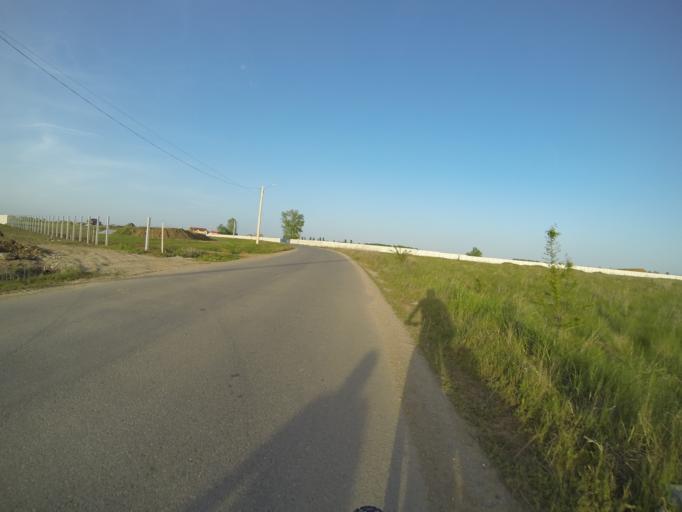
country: RO
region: Dolj
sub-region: Comuna Carcea
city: Carcea
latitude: 44.3222
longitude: 23.8817
